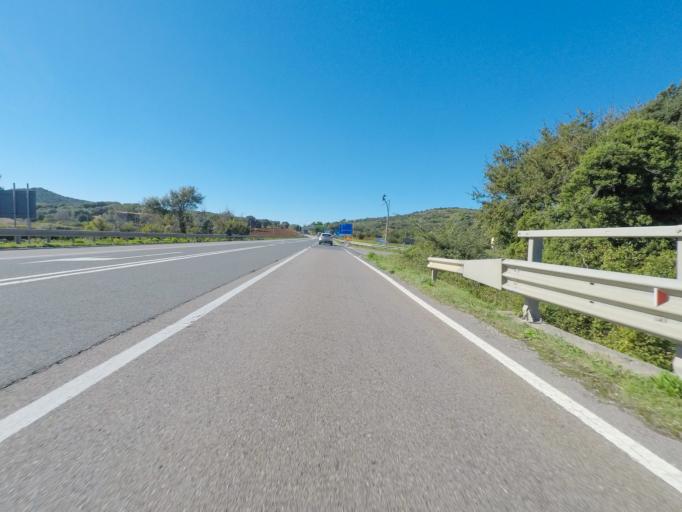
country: IT
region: Tuscany
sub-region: Provincia di Grosseto
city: Orbetello Scalo
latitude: 42.4179
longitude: 11.3055
